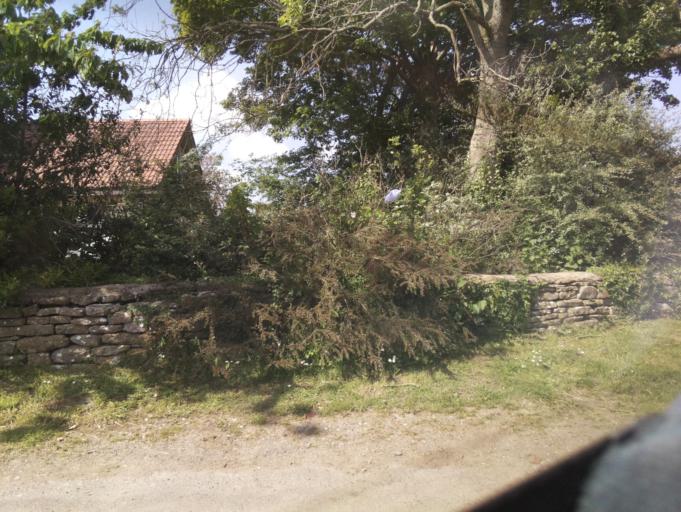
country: GB
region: England
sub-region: South Gloucestershire
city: Horton
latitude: 51.5807
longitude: -2.3146
